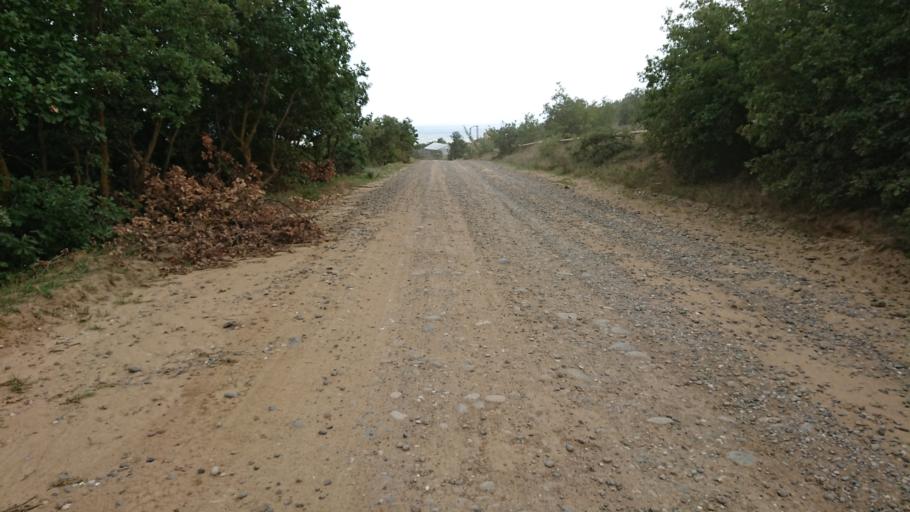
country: RU
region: Dagestan
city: Derbent
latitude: 42.0123
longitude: 48.2706
